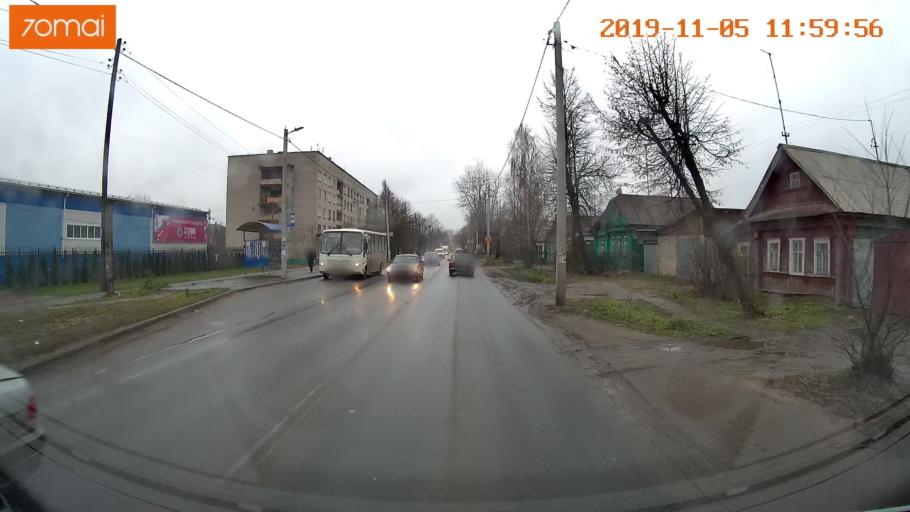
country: RU
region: Ivanovo
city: Kokhma
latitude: 56.9770
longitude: 41.0493
